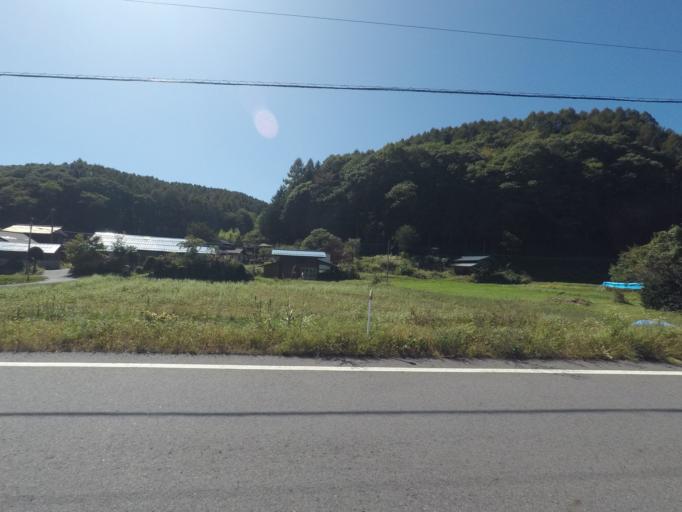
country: JP
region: Nagano
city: Tatsuno
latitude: 35.9714
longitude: 137.7558
